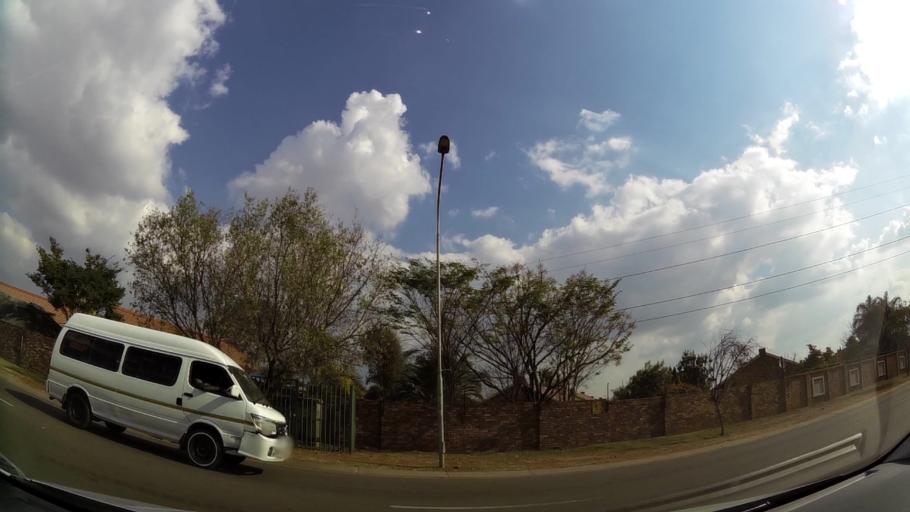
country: ZA
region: Gauteng
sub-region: City of Tshwane Metropolitan Municipality
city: Centurion
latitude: -25.8766
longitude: 28.1939
